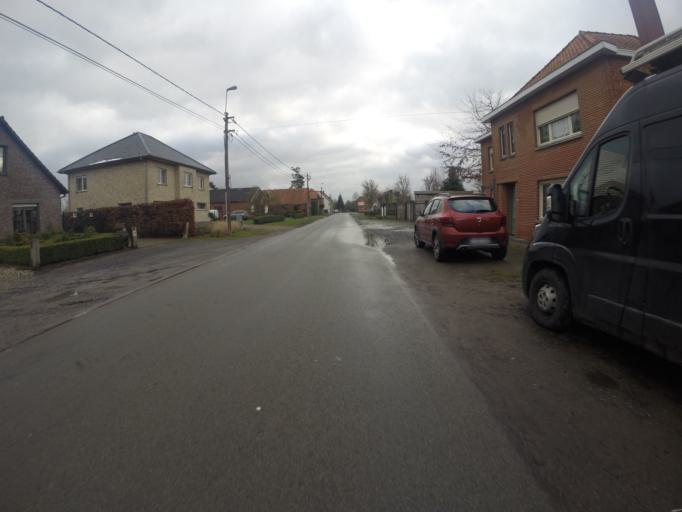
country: BE
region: Flanders
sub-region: Provincie Oost-Vlaanderen
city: Maldegem
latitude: 51.1827
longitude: 3.4571
